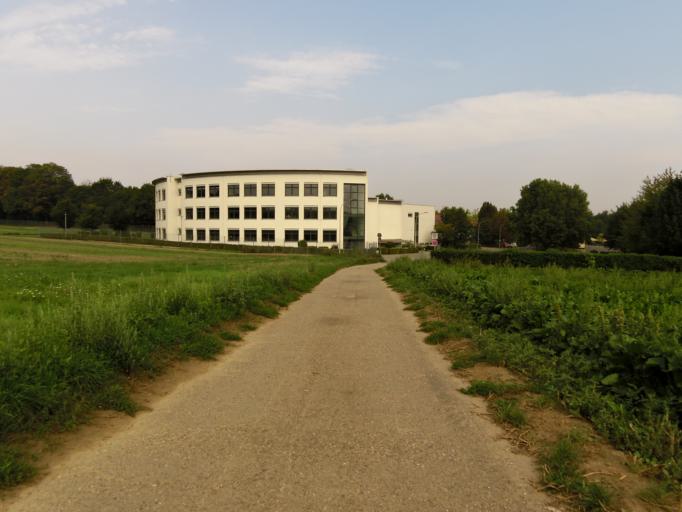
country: DE
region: Rheinland-Pfalz
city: Alzey
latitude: 49.7389
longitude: 8.1220
